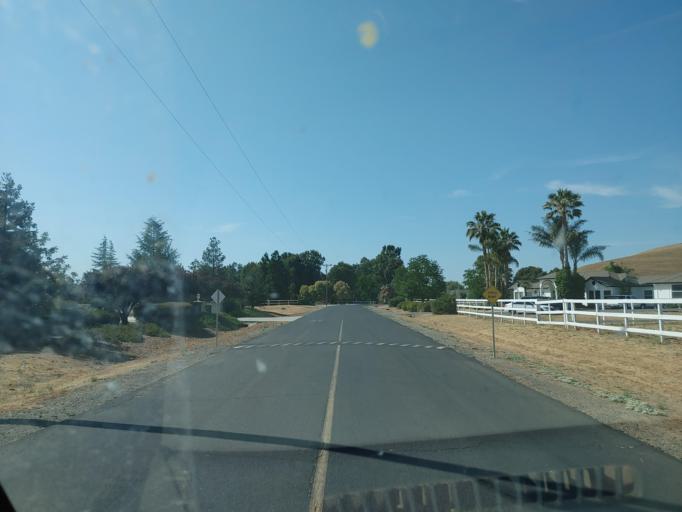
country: US
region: California
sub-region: San Benito County
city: Ridgemark
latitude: 36.8008
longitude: -121.3331
